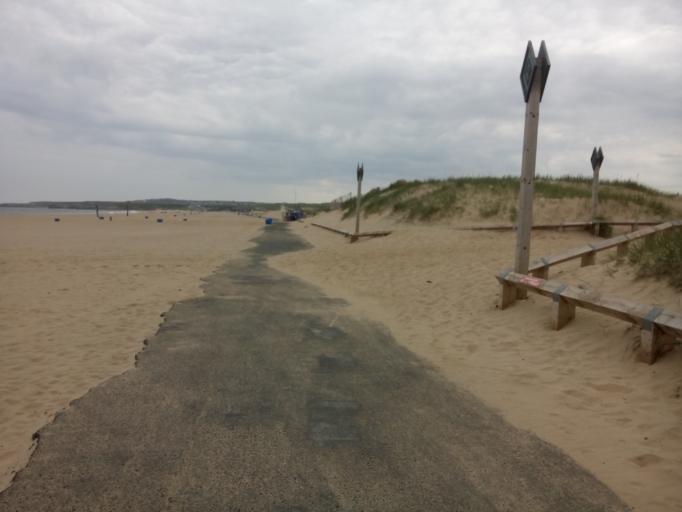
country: GB
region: England
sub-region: South Tyneside
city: South Shields
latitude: 55.0026
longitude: -1.4149
